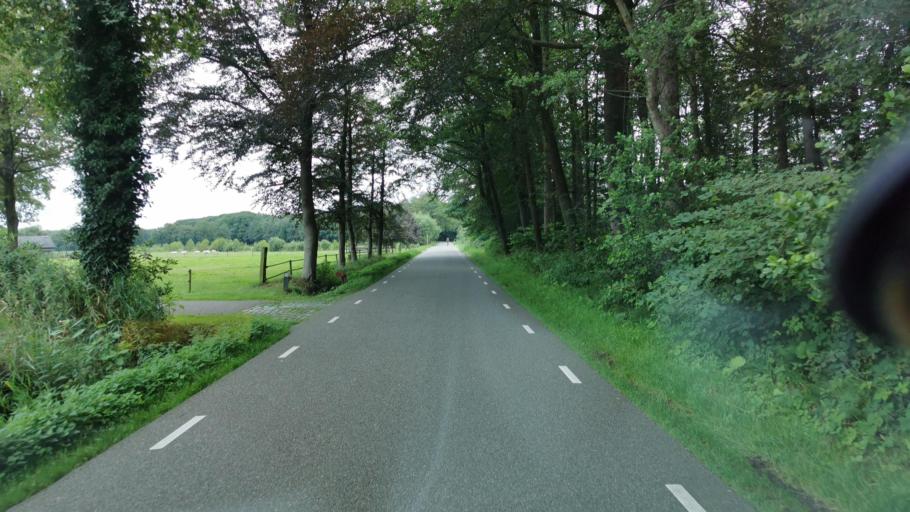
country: NL
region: Overijssel
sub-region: Gemeente Enschede
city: Enschede
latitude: 52.2440
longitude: 6.9415
